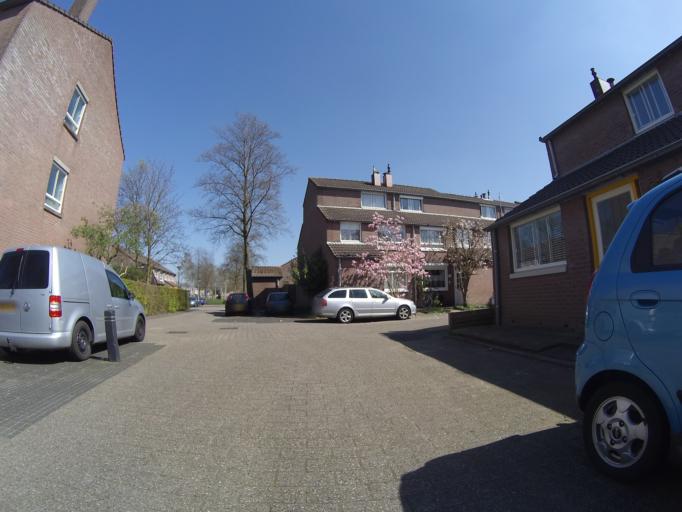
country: NL
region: Utrecht
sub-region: Gemeente Amersfoort
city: Amersfoort
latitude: 52.1738
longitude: 5.3984
